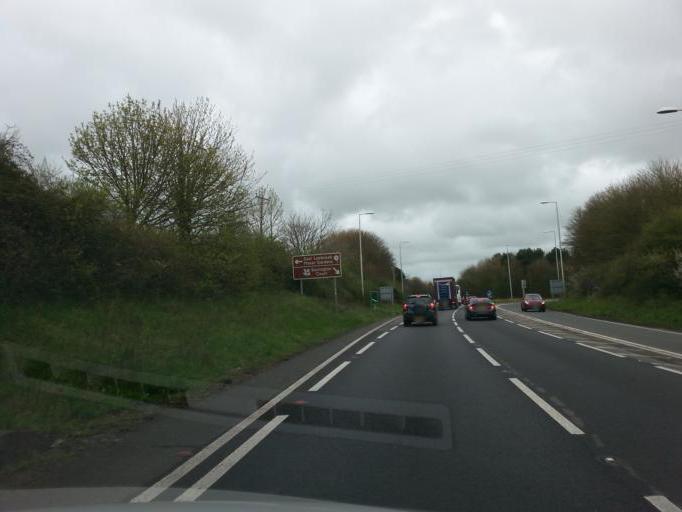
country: GB
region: England
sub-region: Somerset
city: South Petherton
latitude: 50.9421
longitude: -2.8051
